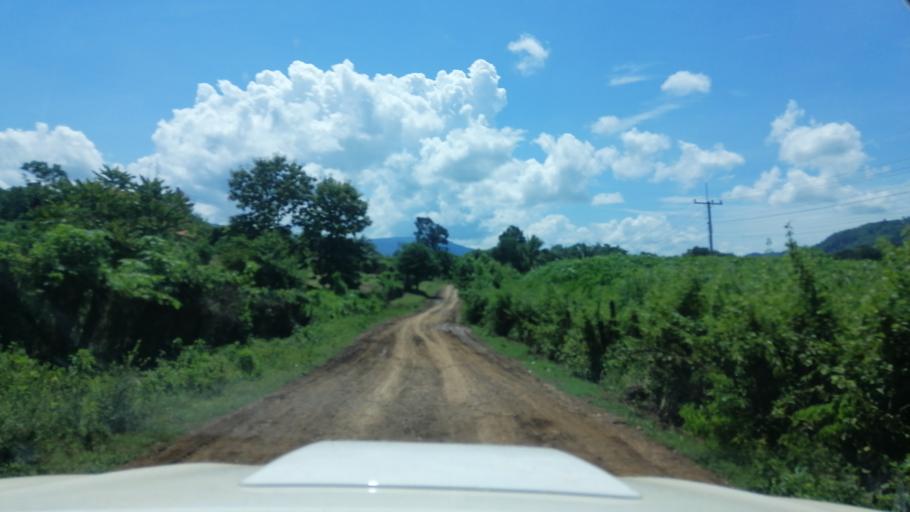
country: TH
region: Uttaradit
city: Ban Khok
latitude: 18.1310
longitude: 101.2674
